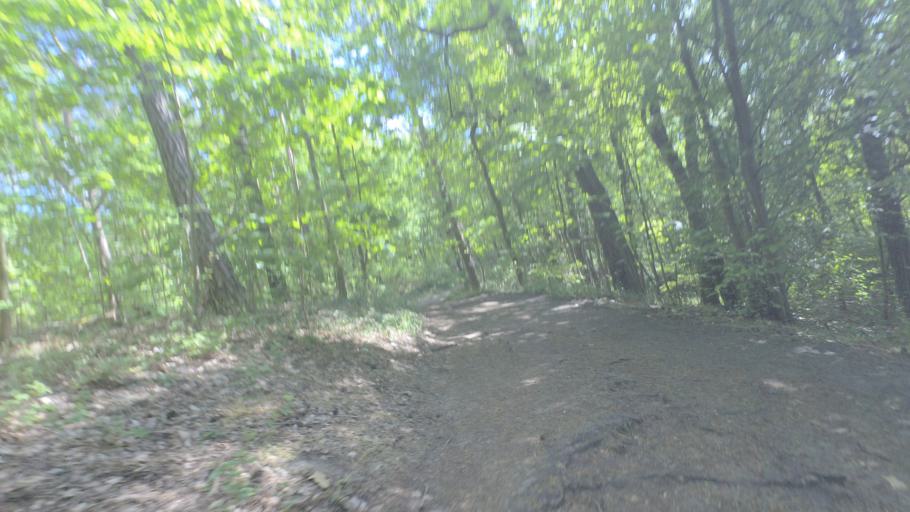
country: DE
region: Brandenburg
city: Erkner
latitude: 52.4273
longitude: 13.7639
